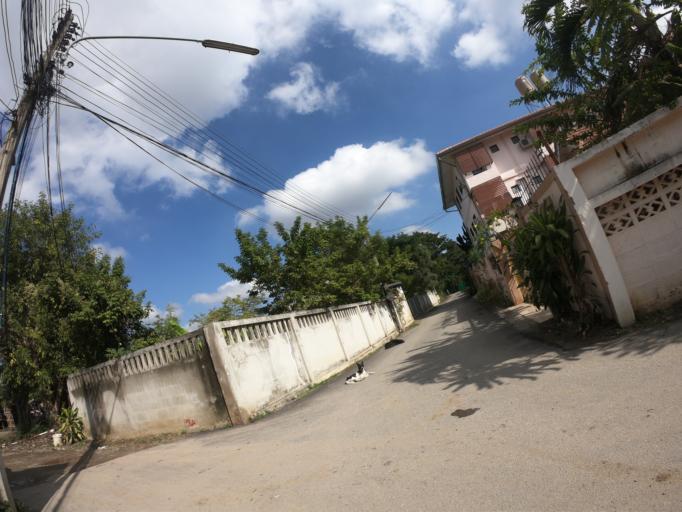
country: TH
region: Chiang Mai
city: Chiang Mai
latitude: 18.7899
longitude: 99.0349
